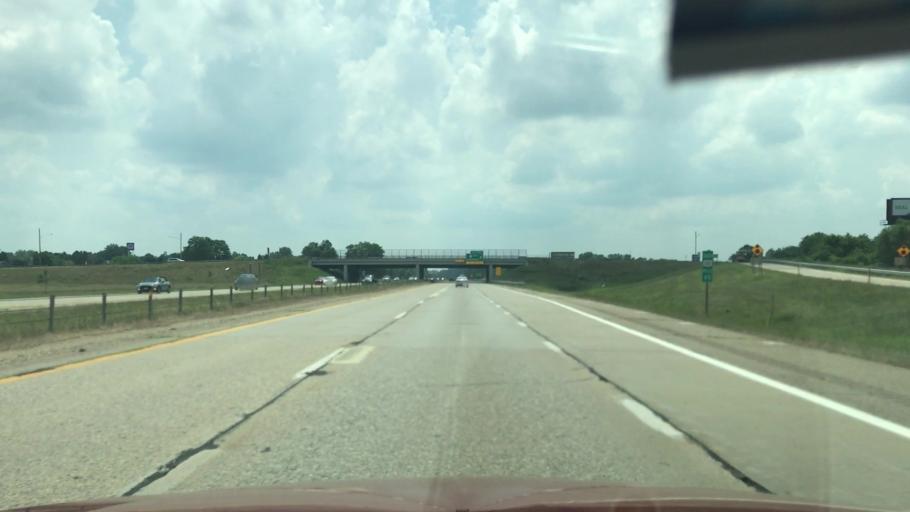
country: US
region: Michigan
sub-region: Allegan County
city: Plainwell
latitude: 42.4521
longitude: -85.6551
